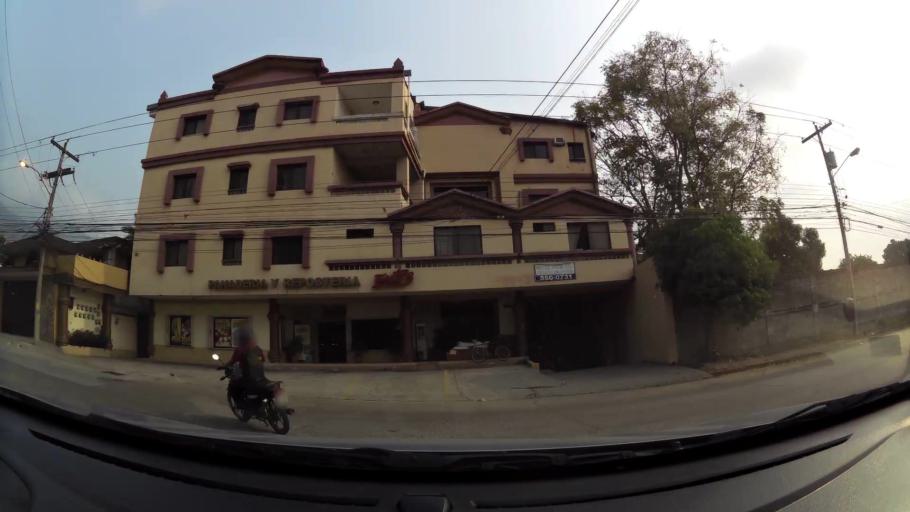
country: HN
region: Cortes
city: Armenta
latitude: 15.4980
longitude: -88.0461
